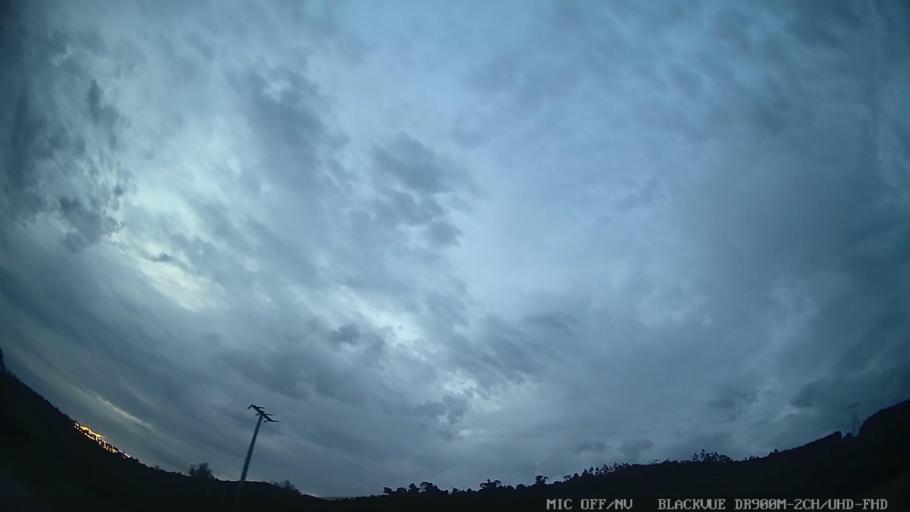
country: BR
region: Sao Paulo
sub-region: Amparo
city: Amparo
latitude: -22.8287
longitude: -46.7681
